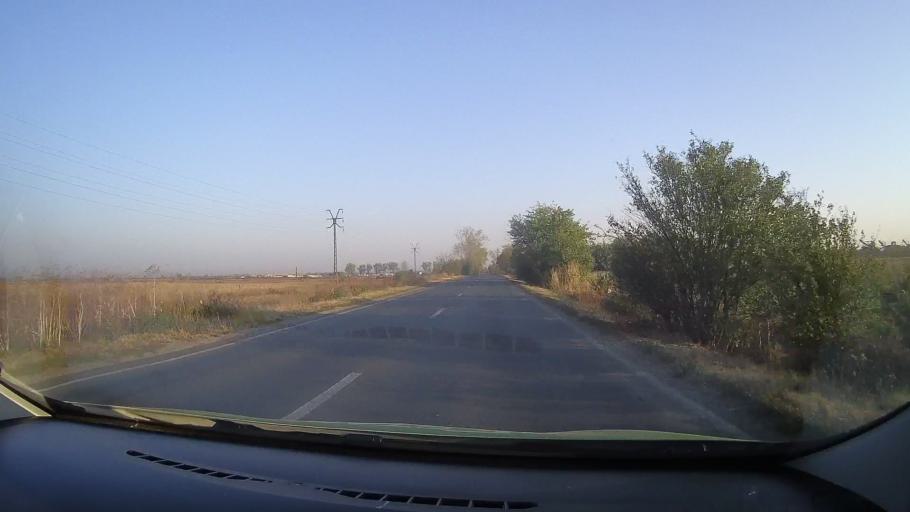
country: RO
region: Arad
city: Arad
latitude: 46.2207
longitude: 21.3205
